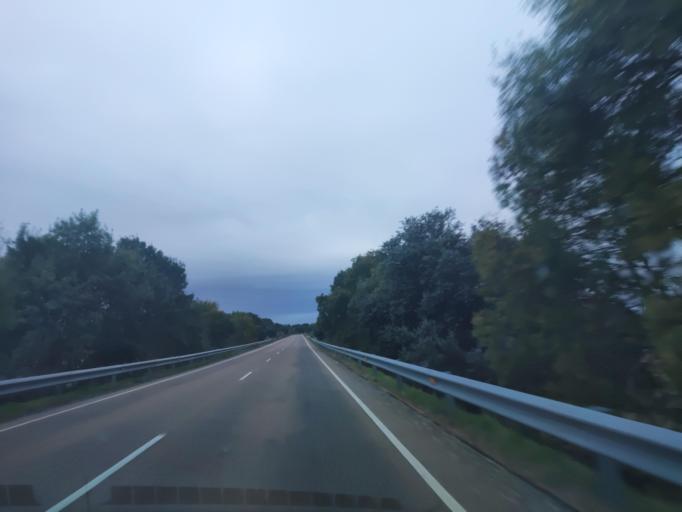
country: ES
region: Castille and Leon
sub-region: Provincia de Salamanca
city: Lumbrales
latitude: 40.9450
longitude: -6.7619
